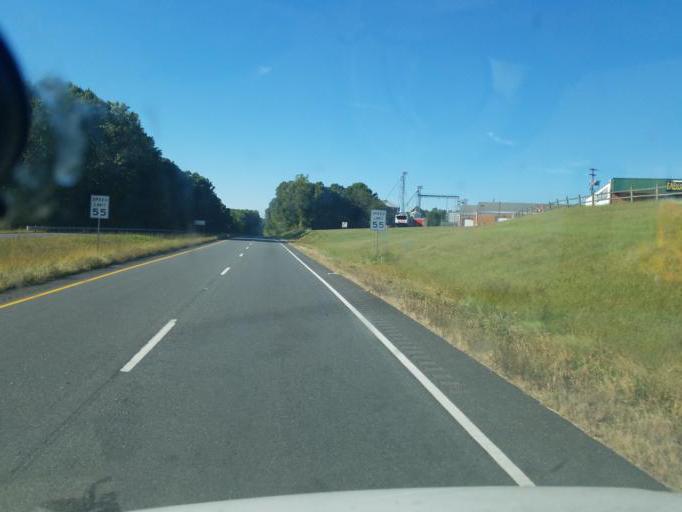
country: US
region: Virginia
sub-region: Madison County
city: Madison
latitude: 38.3902
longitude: -78.2432
